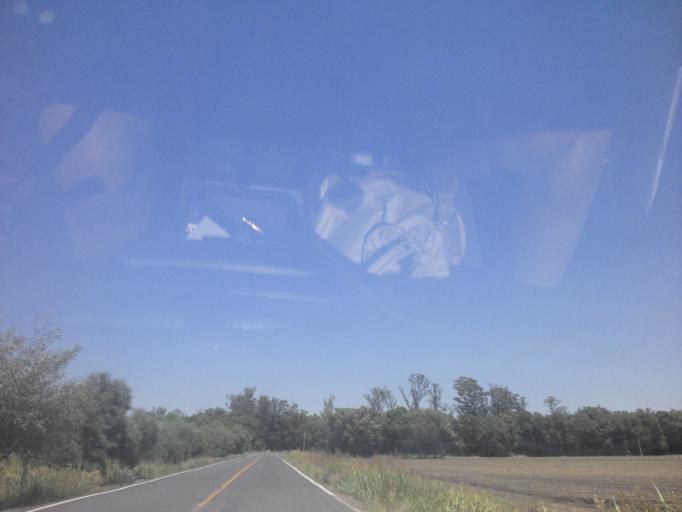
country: MX
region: Jalisco
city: San Diego de Alejandria
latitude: 20.8731
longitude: -101.9854
